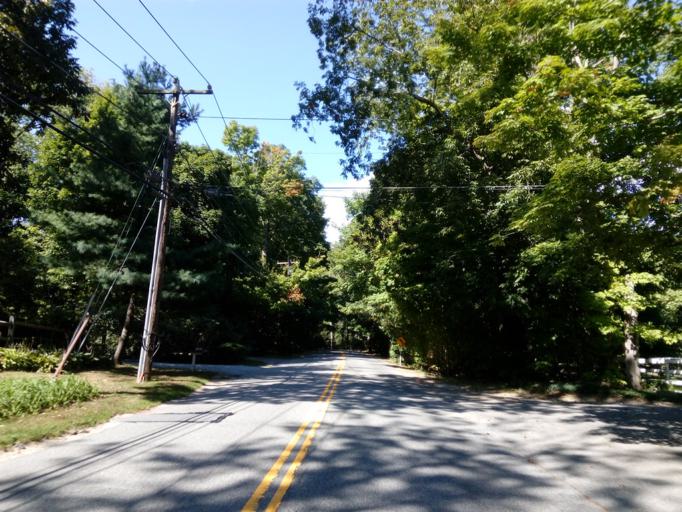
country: US
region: New York
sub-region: Nassau County
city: Laurel Hollow
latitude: 40.8586
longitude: -73.4742
